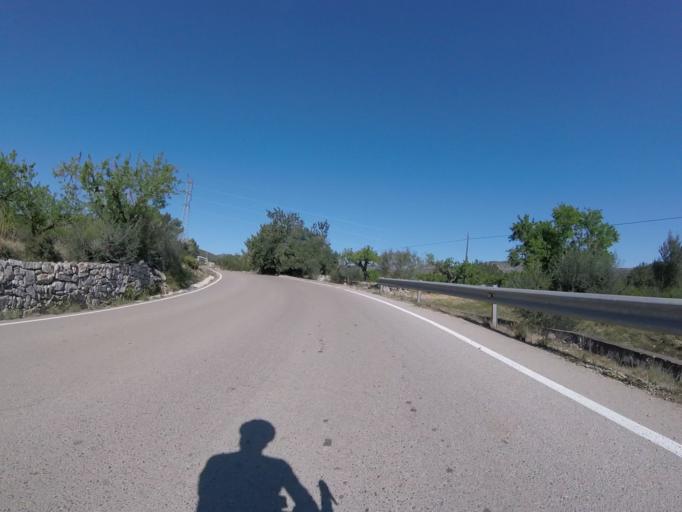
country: ES
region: Valencia
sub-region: Provincia de Castello
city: Santa Magdalena de Pulpis
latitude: 40.3605
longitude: 0.2845
